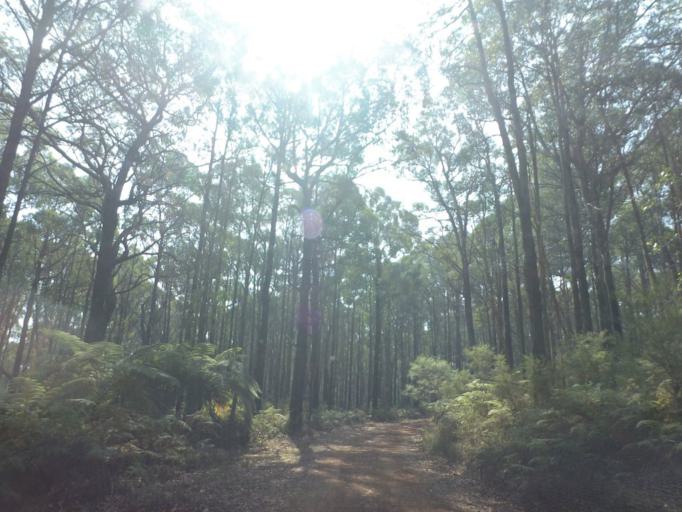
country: AU
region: Victoria
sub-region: Yarra Ranges
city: Millgrove
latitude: -37.5807
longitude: 145.6862
